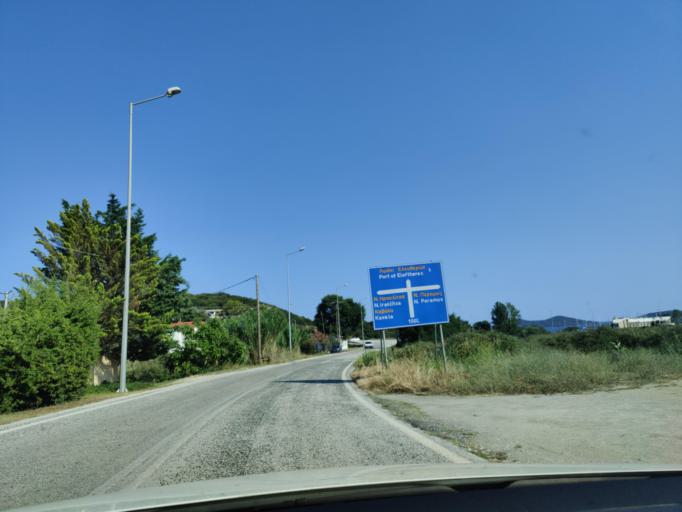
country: GR
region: East Macedonia and Thrace
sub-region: Nomos Kavalas
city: Nea Iraklitsa
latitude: 40.8554
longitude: 24.3129
